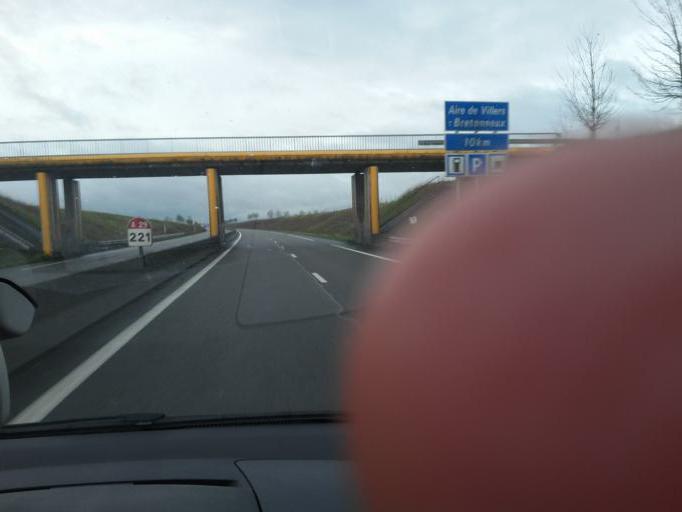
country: FR
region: Picardie
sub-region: Departement de la Somme
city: Harbonnieres
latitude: 49.8600
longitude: 2.6602
